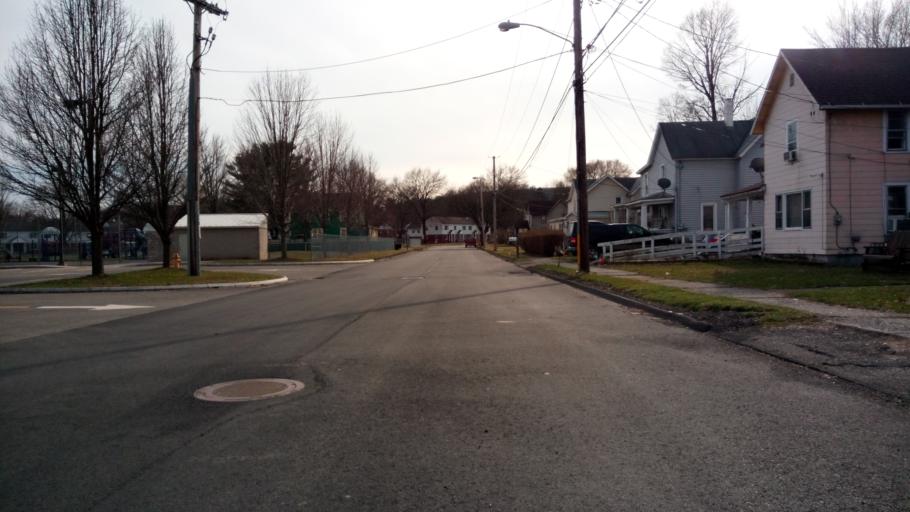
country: US
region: New York
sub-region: Chemung County
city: Elmira Heights
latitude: 42.1126
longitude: -76.8236
